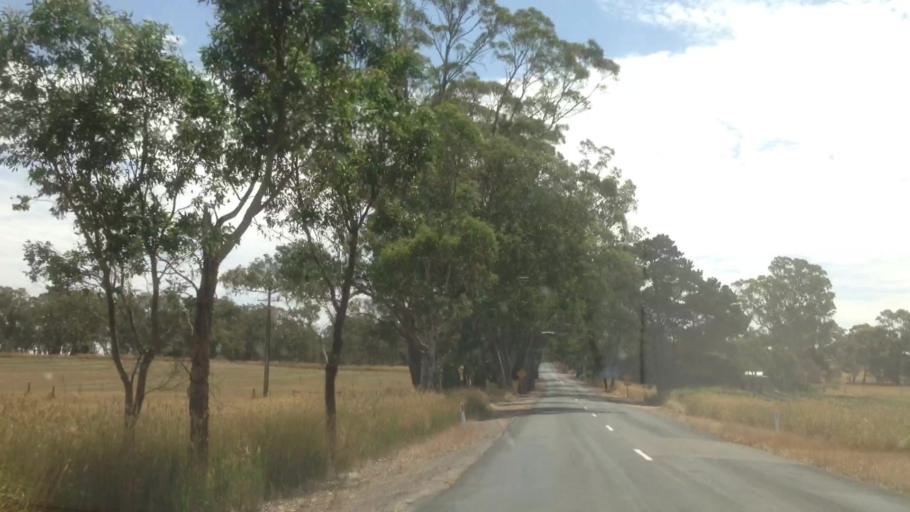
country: AU
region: South Australia
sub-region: Adelaide Hills
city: Birdwood
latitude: -34.7909
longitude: 138.9577
